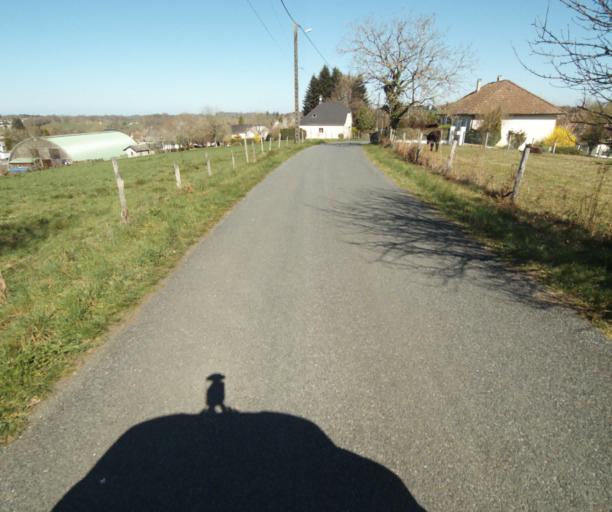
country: FR
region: Limousin
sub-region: Departement de la Correze
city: Seilhac
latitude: 45.3676
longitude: 1.7206
